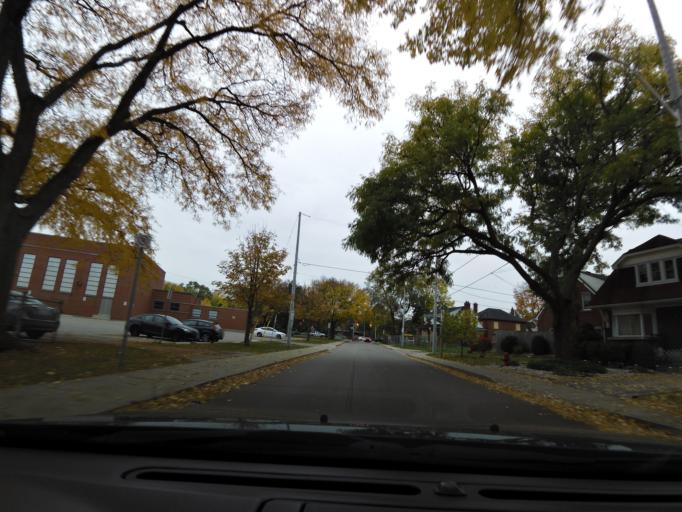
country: CA
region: Ontario
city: Hamilton
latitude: 43.2591
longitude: -79.9136
